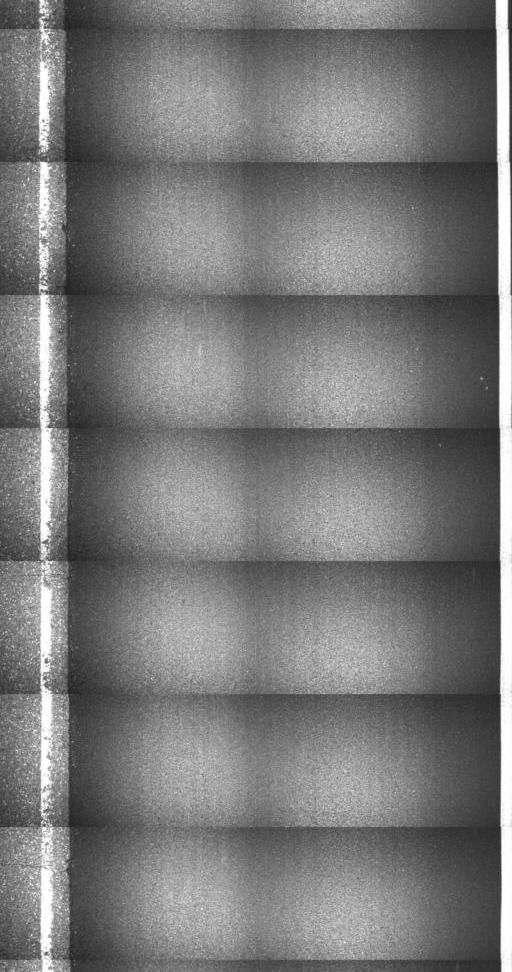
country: US
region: Vermont
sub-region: Lamoille County
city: Hyde Park
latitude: 44.5870
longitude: -72.6027
